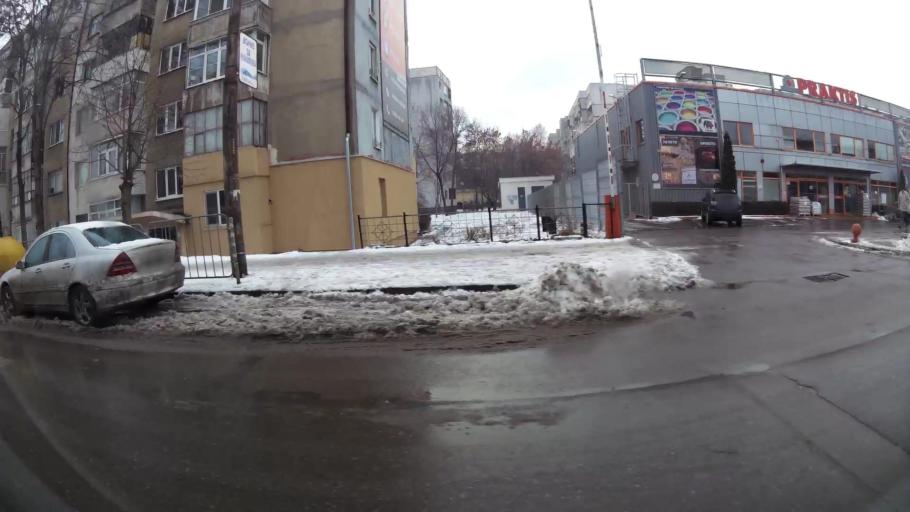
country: BG
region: Sofia-Capital
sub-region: Stolichna Obshtina
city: Sofia
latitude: 42.7109
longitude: 23.3508
